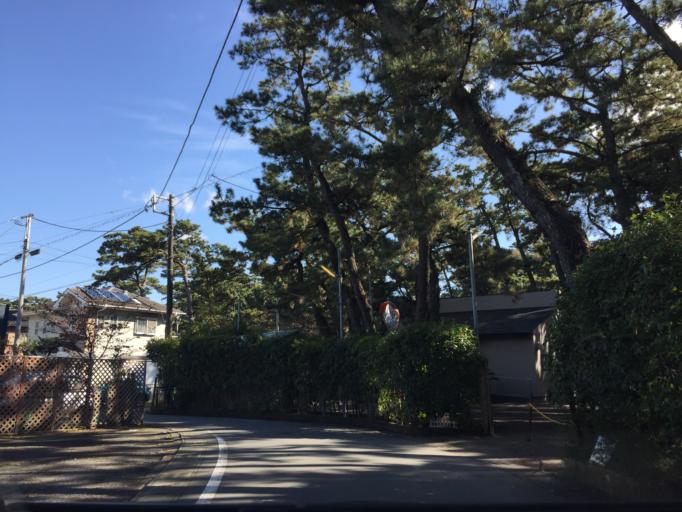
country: JP
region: Shizuoka
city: Numazu
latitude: 35.0756
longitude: 138.8609
